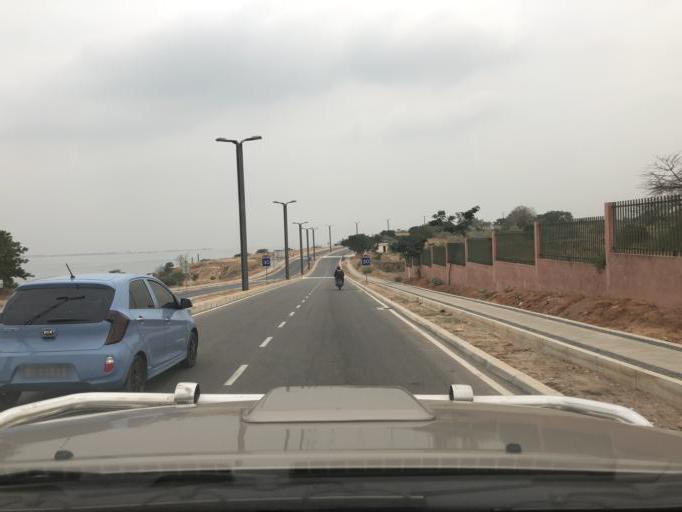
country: AO
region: Luanda
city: Luanda
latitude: -8.8965
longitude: 13.1754
